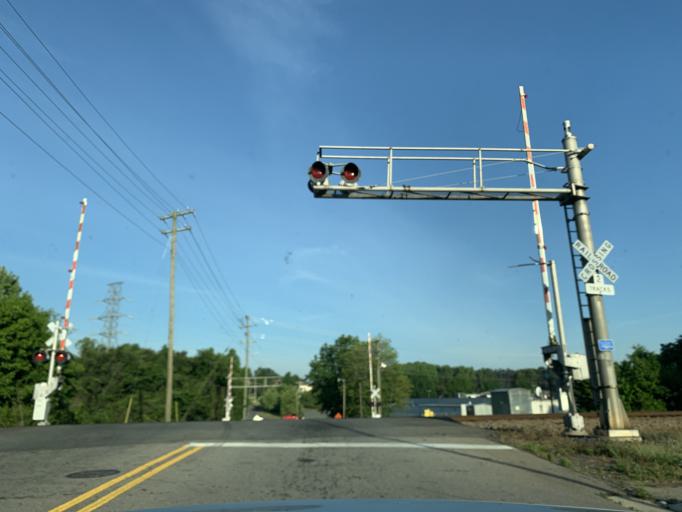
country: US
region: North Carolina
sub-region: Rockingham County
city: Reidsville
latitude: 36.3391
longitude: -79.6552
